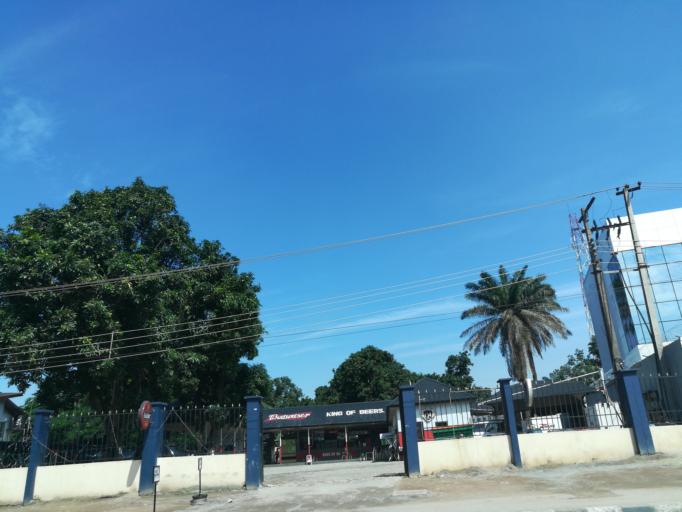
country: NG
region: Lagos
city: Ikeja
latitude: 6.6028
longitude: 3.3447
